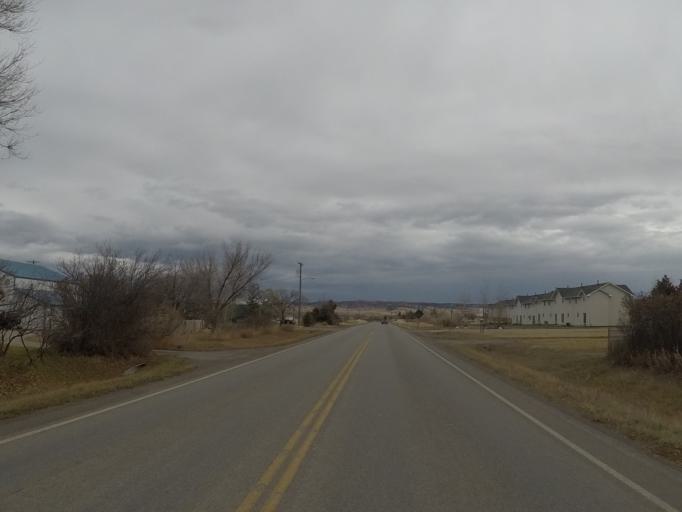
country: US
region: Montana
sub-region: Sweet Grass County
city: Big Timber
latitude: 45.8405
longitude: -109.9460
